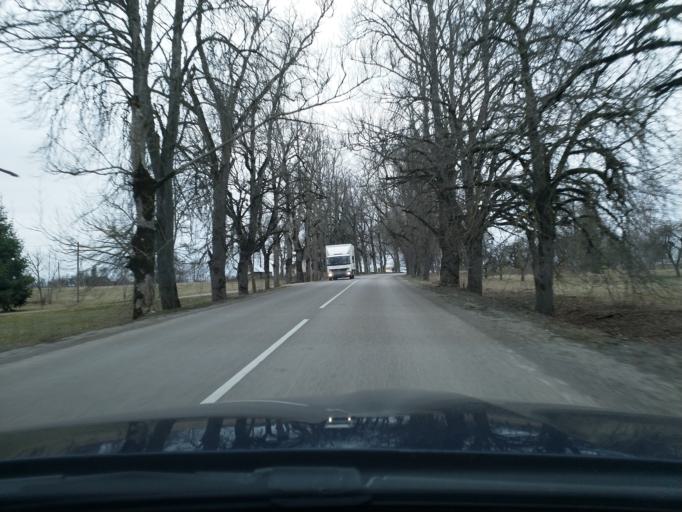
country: LV
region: Talsu Rajons
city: Sabile
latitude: 56.9501
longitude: 22.3728
